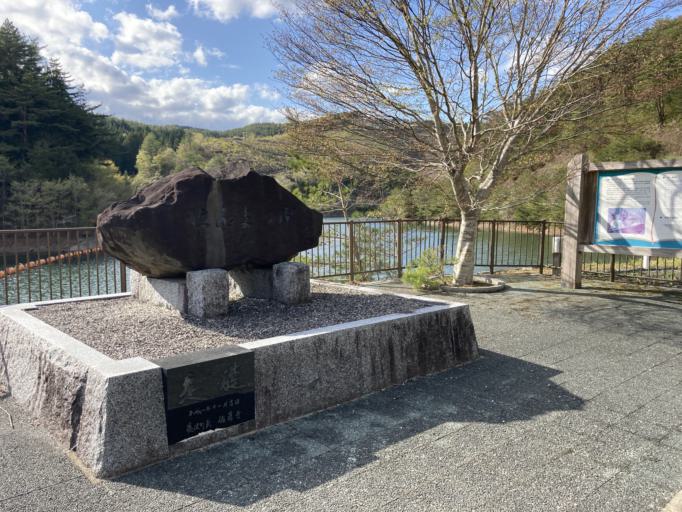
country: JP
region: Iwate
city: Ichinoseki
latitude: 38.8012
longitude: 141.4139
